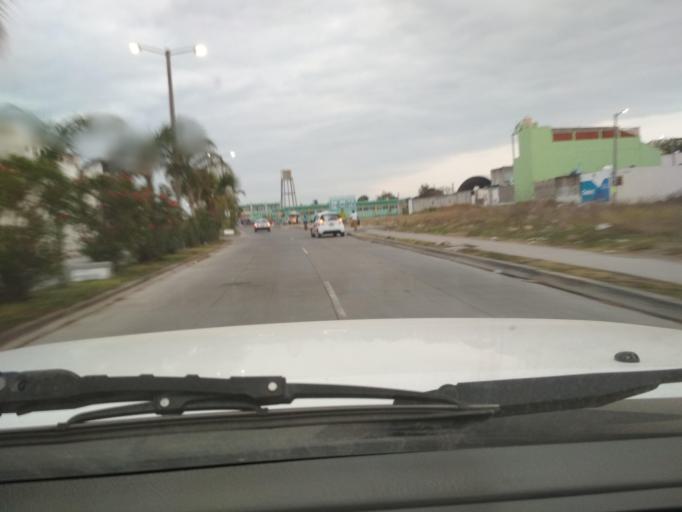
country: MX
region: Veracruz
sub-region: Medellin
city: Fraccionamiento Arboledas San Ramon
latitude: 19.0967
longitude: -96.1632
